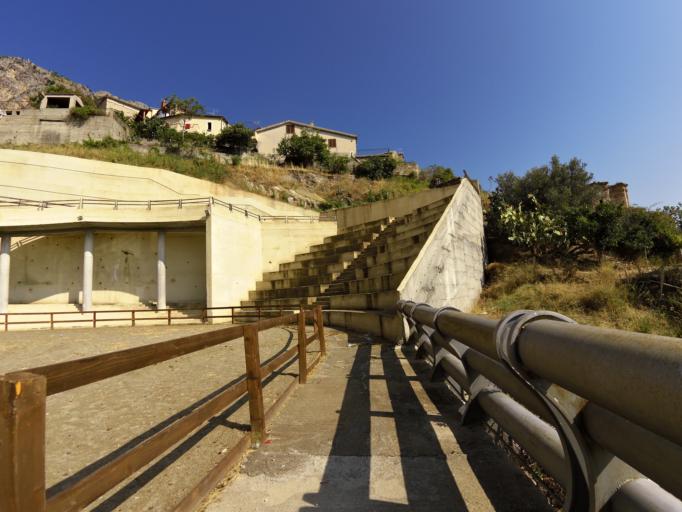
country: IT
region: Calabria
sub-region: Provincia di Reggio Calabria
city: Stilo
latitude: 38.4777
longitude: 16.4699
